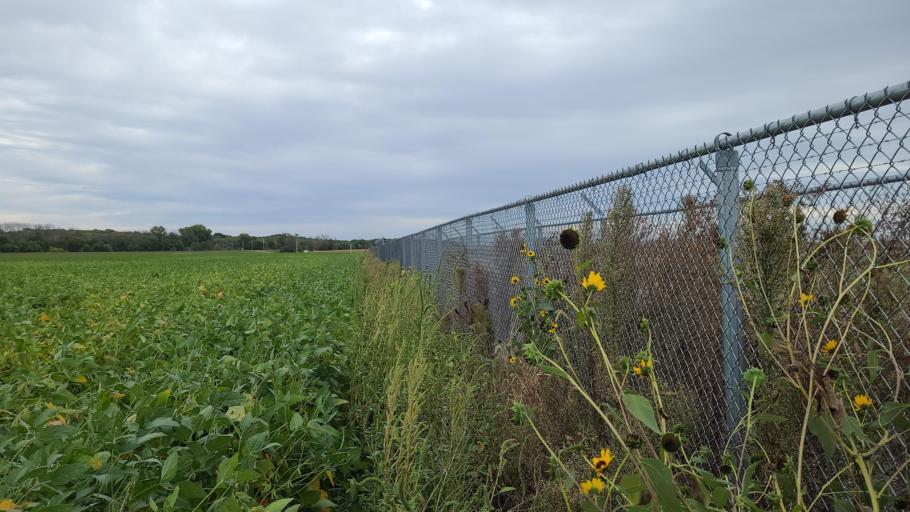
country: US
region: Kansas
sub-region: Douglas County
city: Lawrence
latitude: 39.0162
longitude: -95.2152
